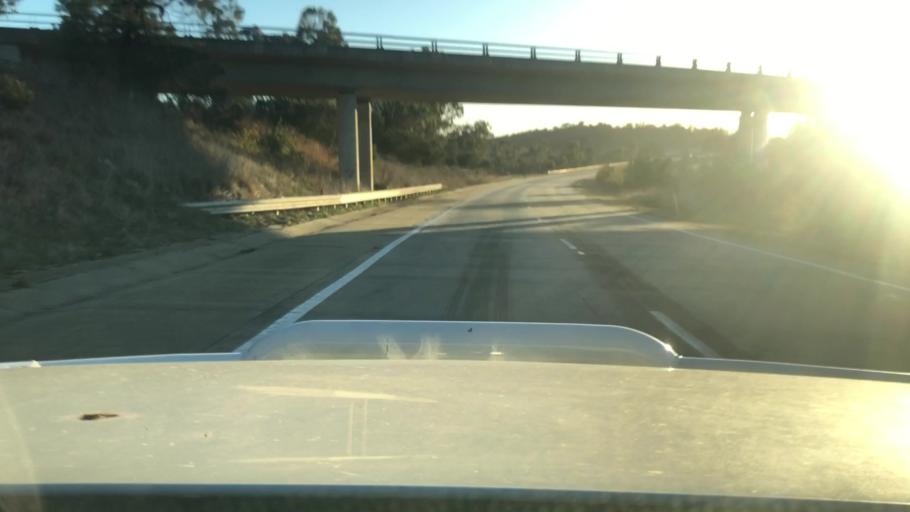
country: AU
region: New South Wales
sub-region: Goulburn Mulwaree
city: Goulburn
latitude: -34.7428
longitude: 149.7714
